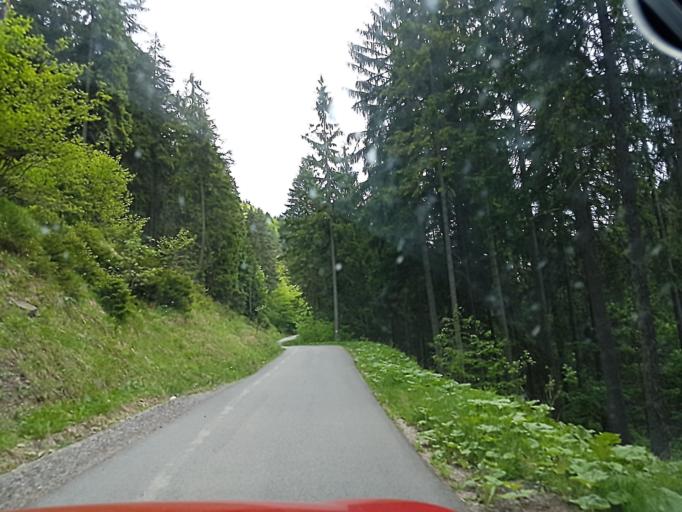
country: SK
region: Zilinsky
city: Ruzomberok
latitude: 49.0591
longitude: 19.2754
